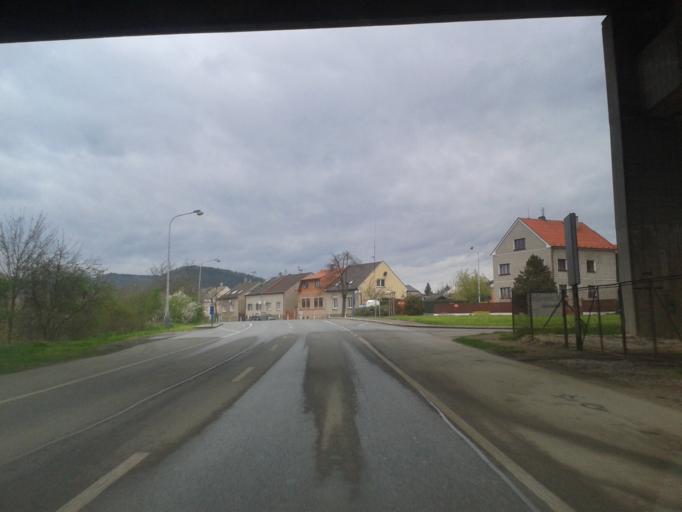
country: CZ
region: Central Bohemia
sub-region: Okres Beroun
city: Beroun
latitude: 49.9622
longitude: 14.0861
